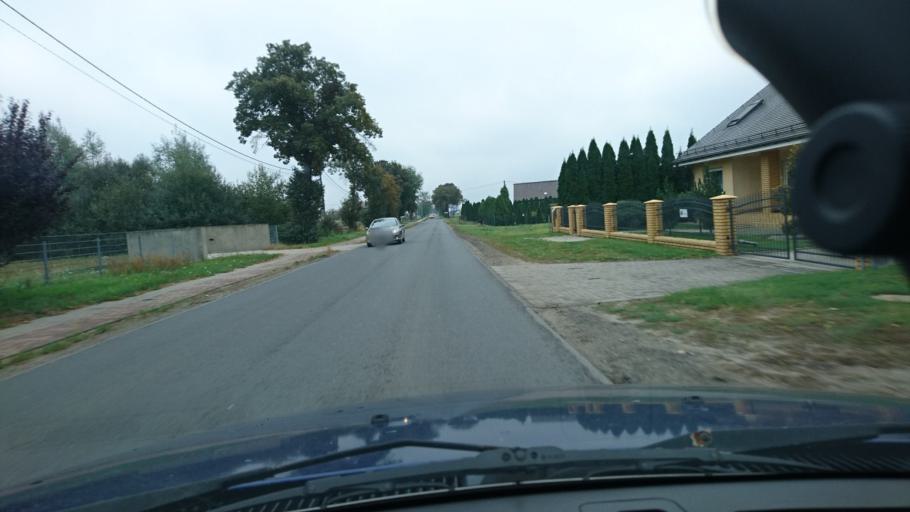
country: PL
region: Greater Poland Voivodeship
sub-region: Powiat ostrowski
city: Odolanow
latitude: 51.5757
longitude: 17.6435
